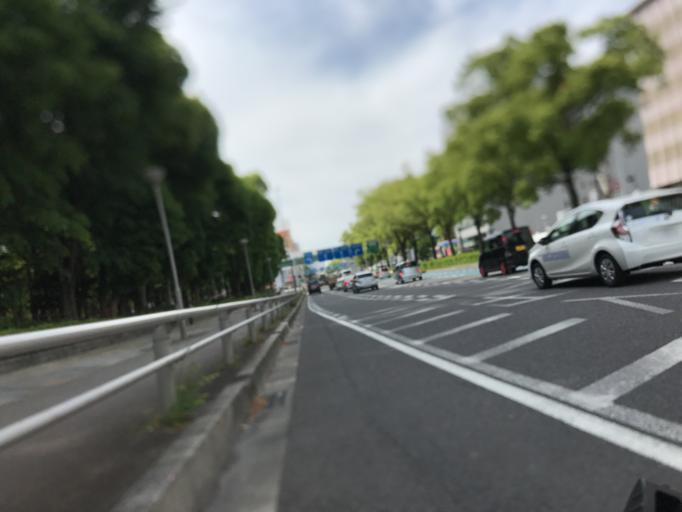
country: JP
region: Aichi
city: Nagoya-shi
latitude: 35.1647
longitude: 136.8980
